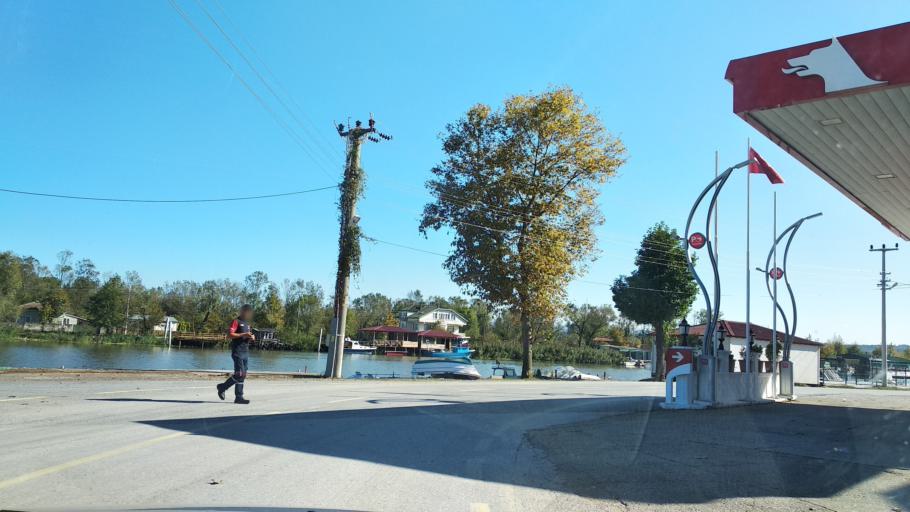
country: TR
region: Sakarya
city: Karasu
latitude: 41.1183
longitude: 30.6449
